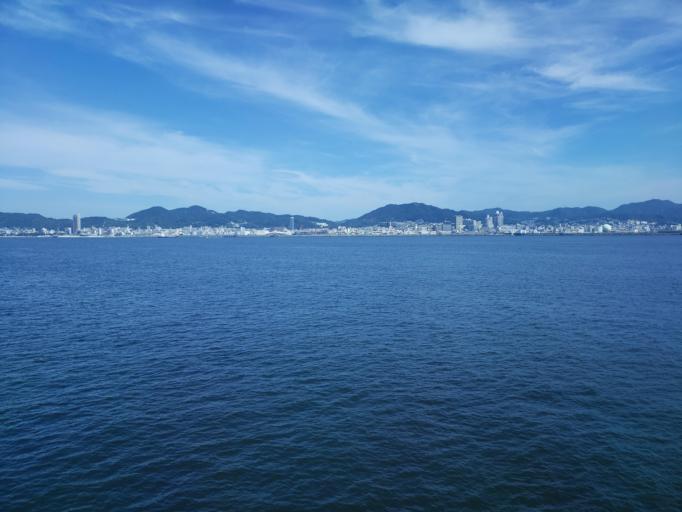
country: JP
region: Hyogo
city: Kobe
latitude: 34.6291
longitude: 135.1558
